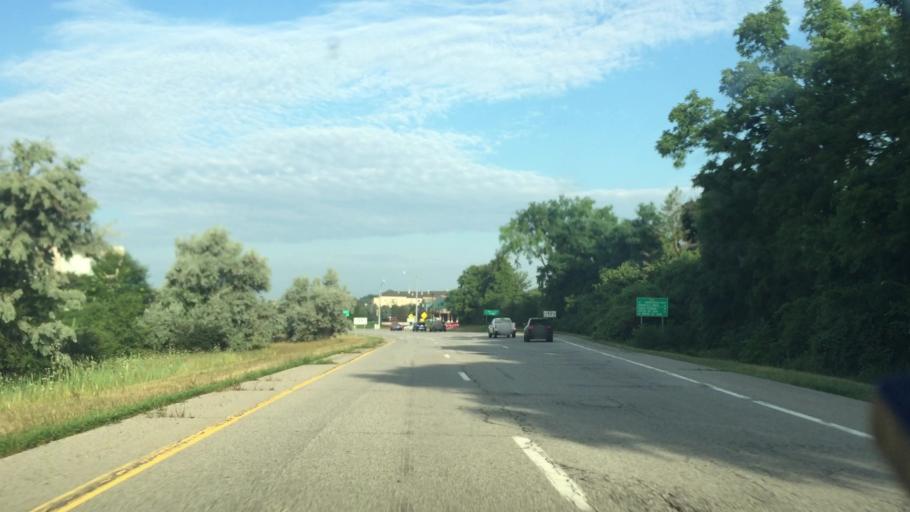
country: US
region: Michigan
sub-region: Oakland County
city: Bloomfield Hills
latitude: 42.6065
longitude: -83.2454
